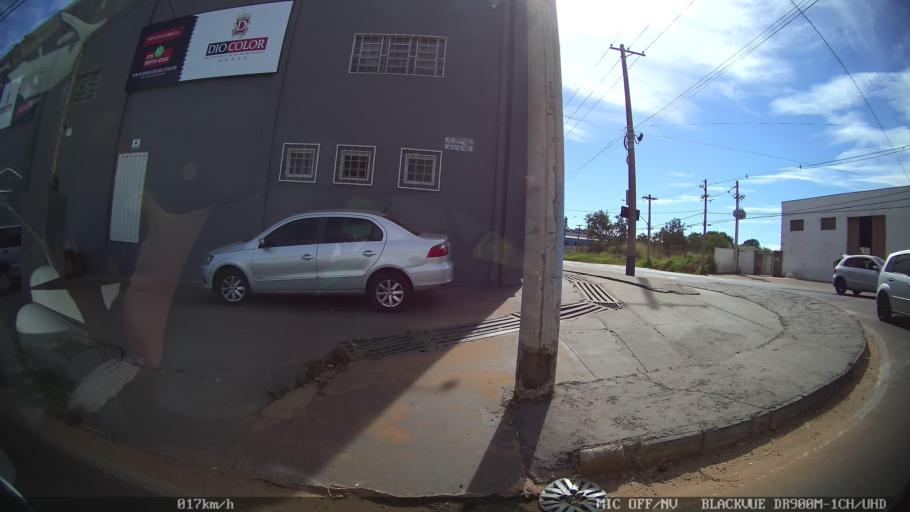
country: BR
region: Sao Paulo
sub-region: Sao Jose Do Rio Preto
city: Sao Jose do Rio Preto
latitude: -20.8406
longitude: -49.3331
